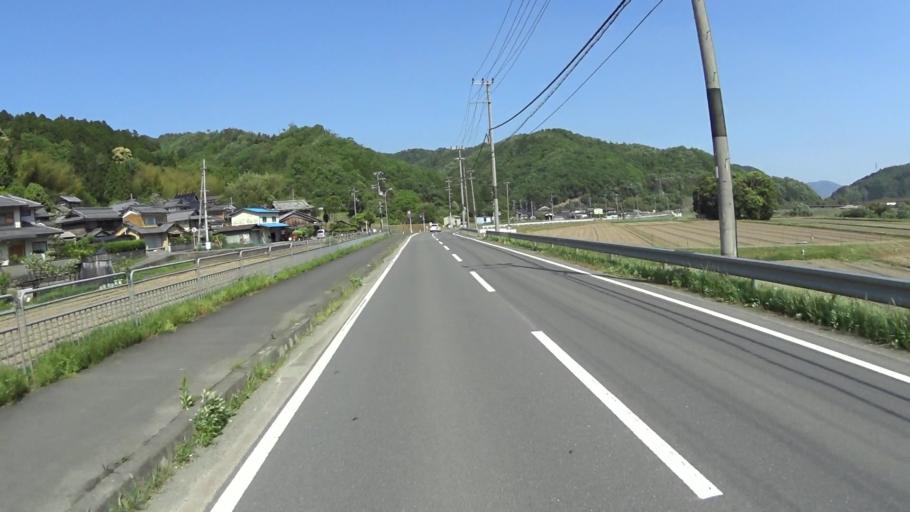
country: JP
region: Kyoto
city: Kameoka
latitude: 35.1273
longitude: 135.4976
